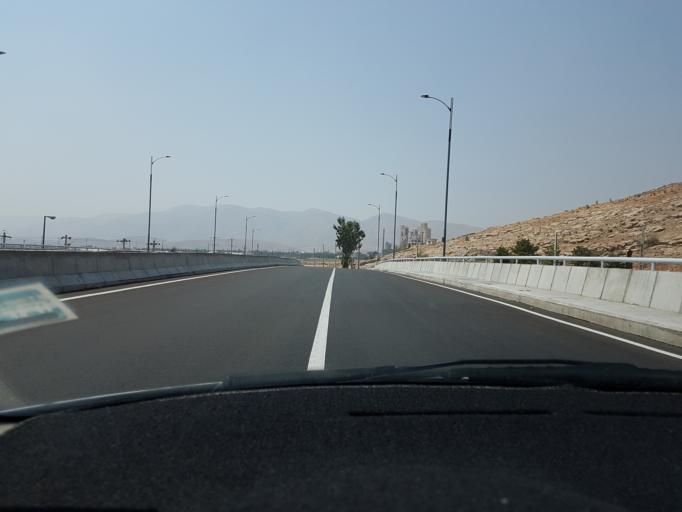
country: IR
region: Fars
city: Shiraz
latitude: 29.6314
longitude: 52.4569
